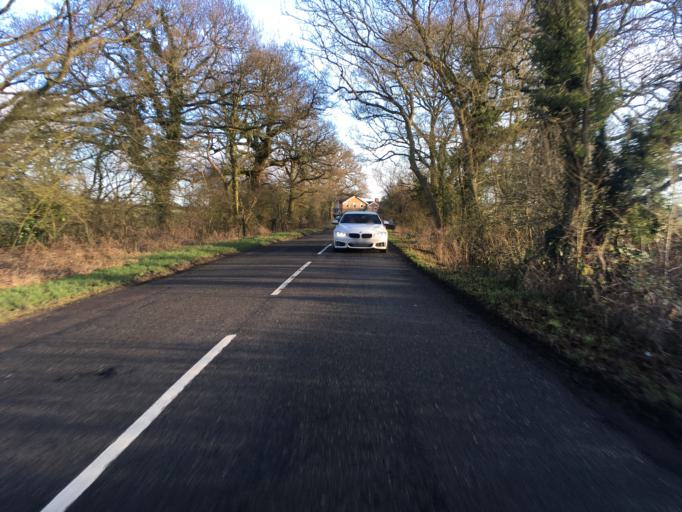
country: GB
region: England
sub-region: Warwickshire
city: Stratford-upon-Avon
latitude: 52.2393
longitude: -1.7035
